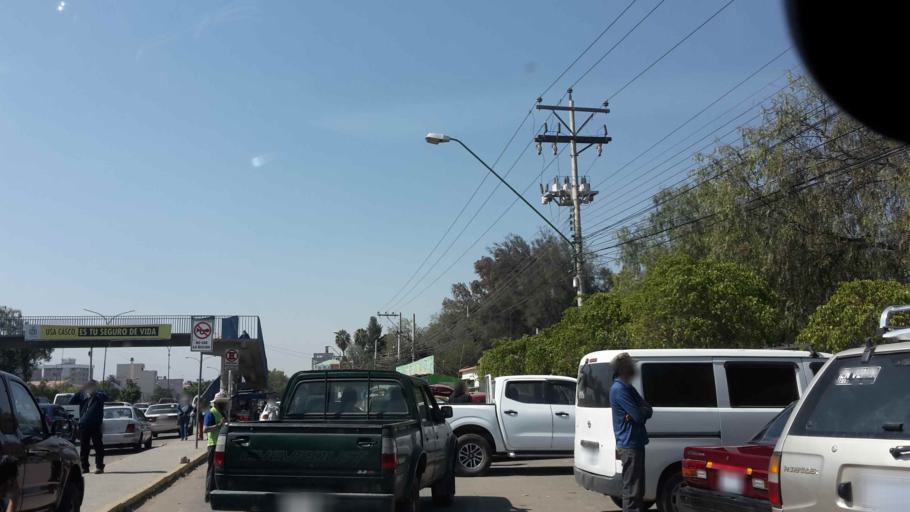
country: BO
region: Cochabamba
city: Cochabamba
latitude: -17.3925
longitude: -66.2055
